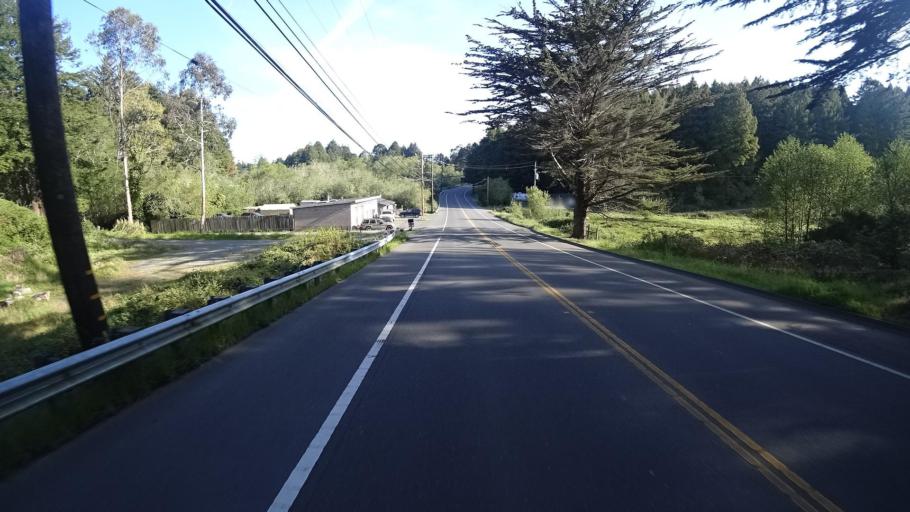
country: US
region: California
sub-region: Humboldt County
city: Bayview
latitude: 40.7683
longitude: -124.1757
